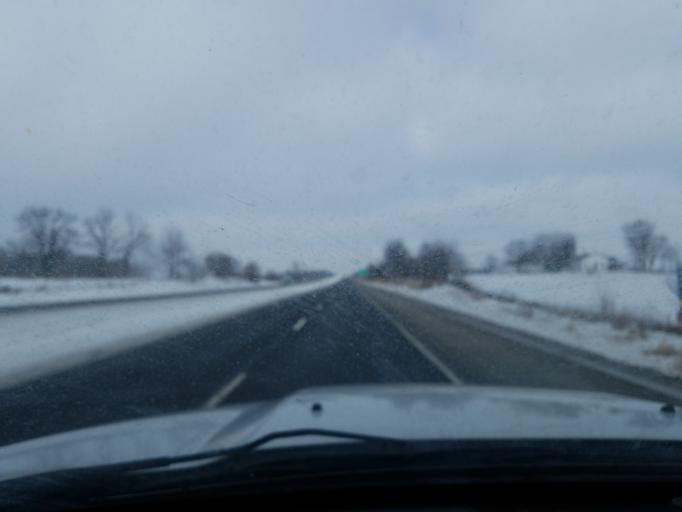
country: US
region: Indiana
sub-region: Marshall County
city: Plymouth
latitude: 41.3272
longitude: -86.2757
